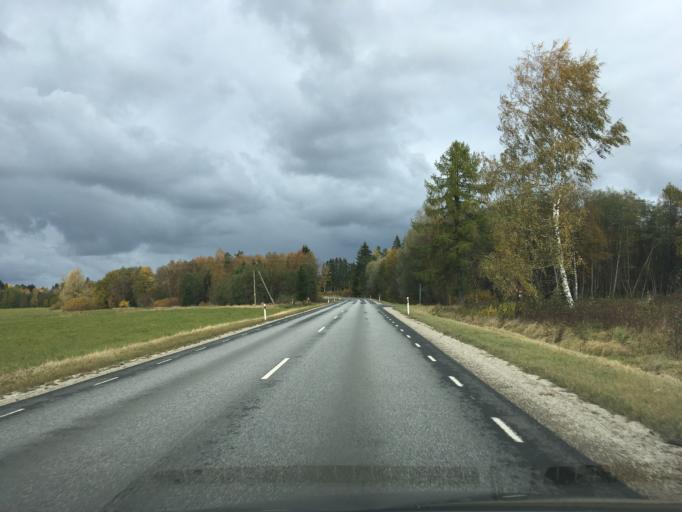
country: EE
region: Harju
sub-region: Anija vald
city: Kehra
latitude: 59.2894
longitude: 25.3754
